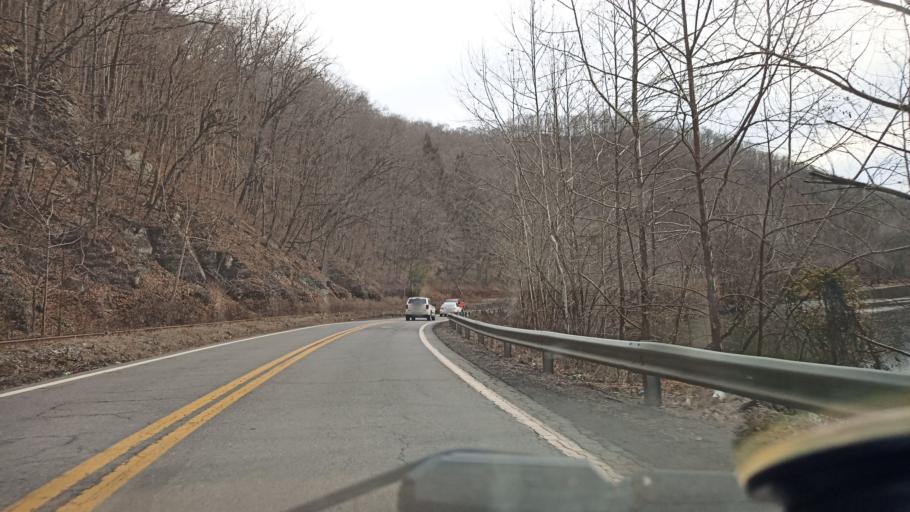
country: US
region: West Virginia
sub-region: Mingo County
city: Gilbert Creek
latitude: 37.6348
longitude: -81.8703
